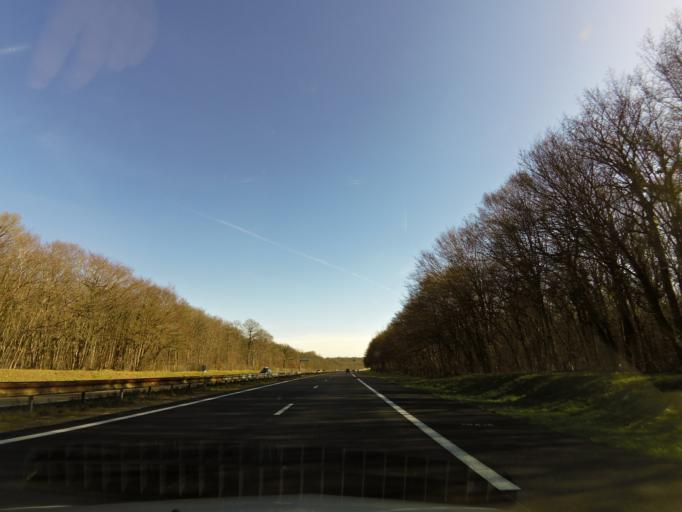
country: FR
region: Bourgogne
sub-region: Departement de l'Yonne
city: Joux-la-Ville
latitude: 47.6934
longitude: 3.8345
